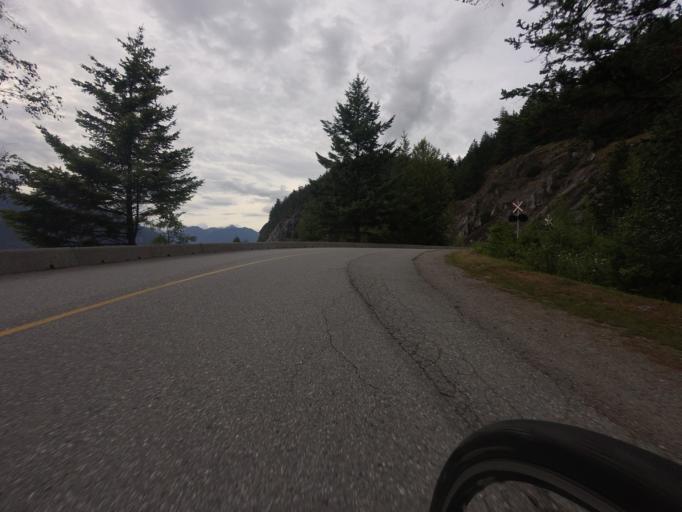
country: CA
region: British Columbia
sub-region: Greater Vancouver Regional District
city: Lions Bay
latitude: 49.5598
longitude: -123.2338
